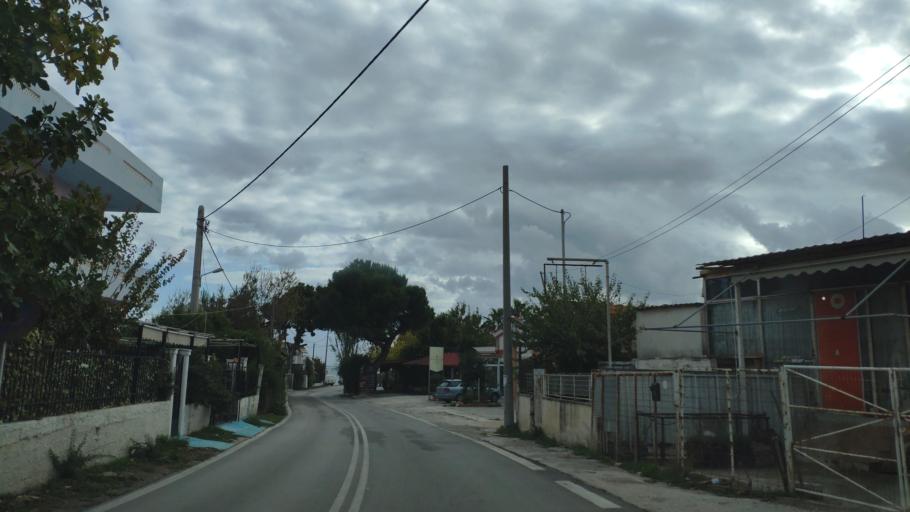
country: GR
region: Attica
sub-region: Nomarchia Anatolikis Attikis
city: Artemida
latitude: 37.9379
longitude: 24.0115
